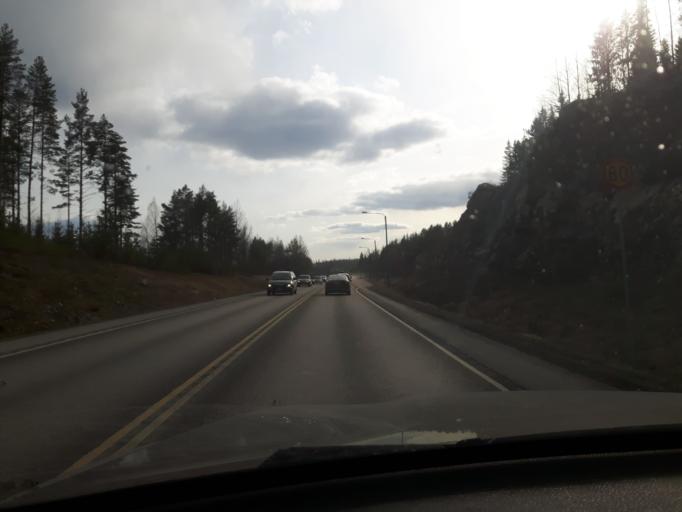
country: FI
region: Pirkanmaa
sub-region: Tampere
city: Kuhmalahti
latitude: 61.7266
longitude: 24.6599
